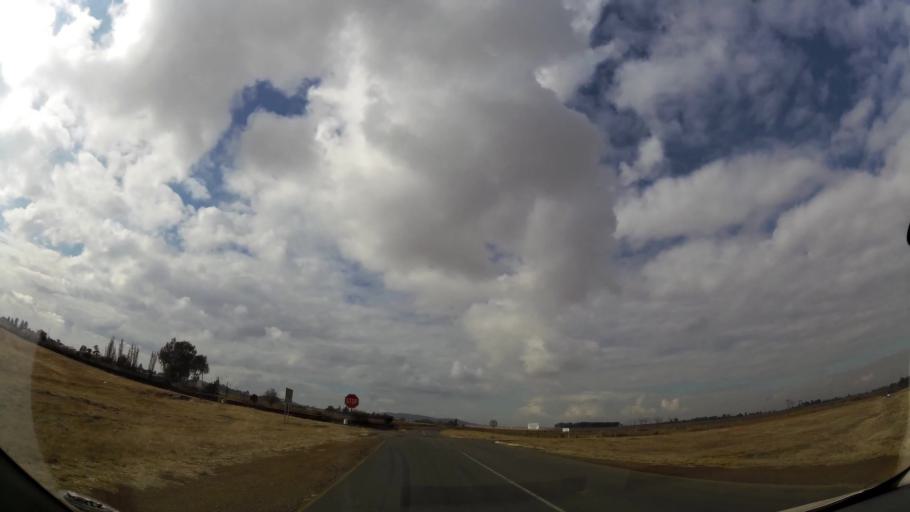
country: ZA
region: Gauteng
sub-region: Sedibeng District Municipality
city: Meyerton
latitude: -26.6193
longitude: 28.0571
